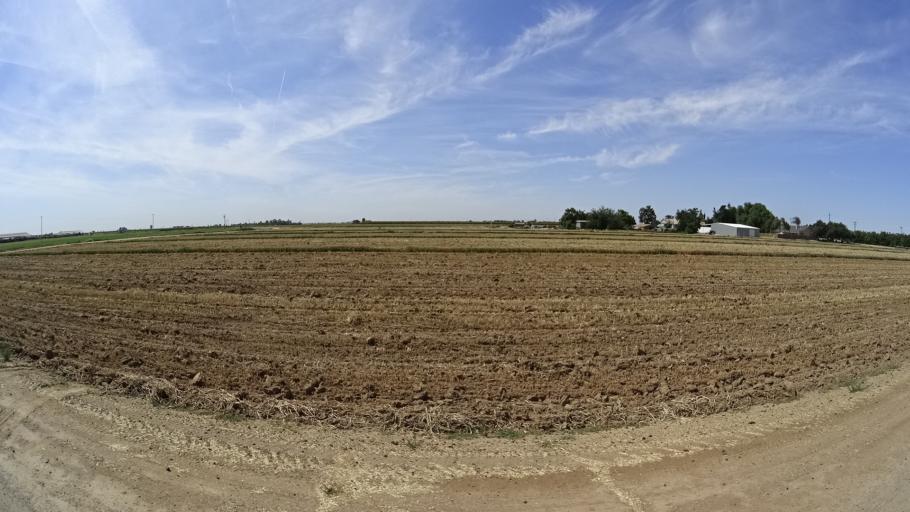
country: US
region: California
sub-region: Kings County
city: Hanford
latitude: 36.3574
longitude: -119.5806
